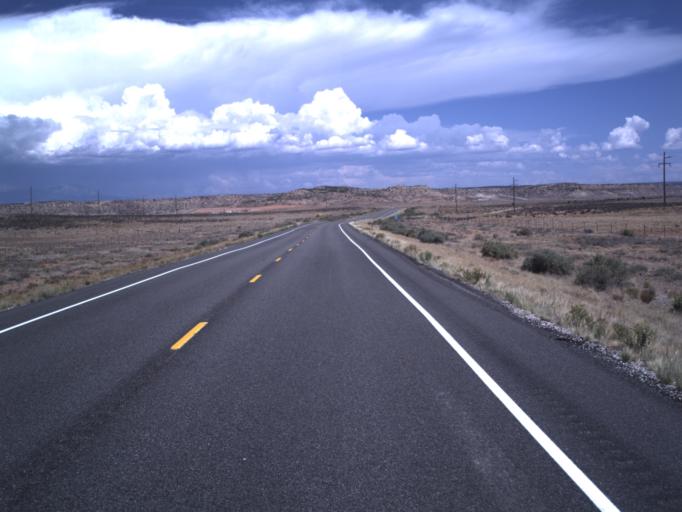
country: US
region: Utah
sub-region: San Juan County
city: Blanding
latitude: 37.3928
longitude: -109.4984
